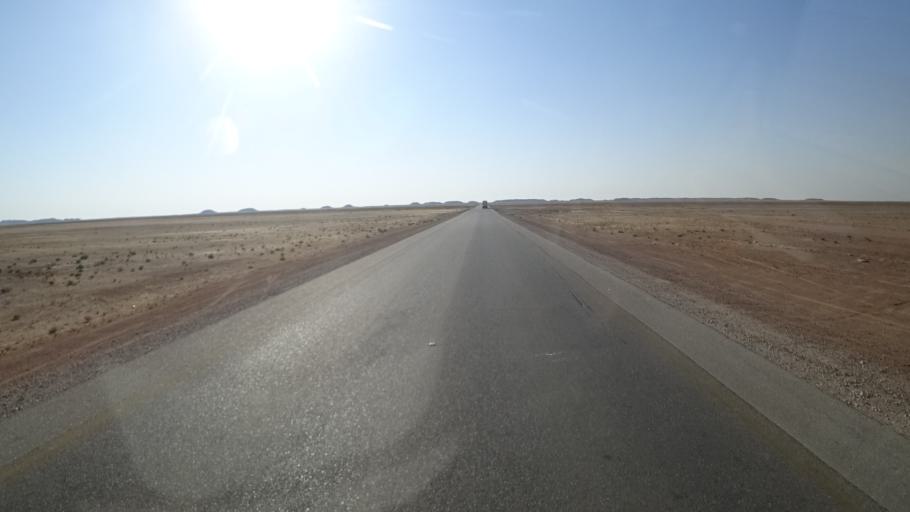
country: OM
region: Zufar
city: Salalah
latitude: 17.6425
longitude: 53.8394
